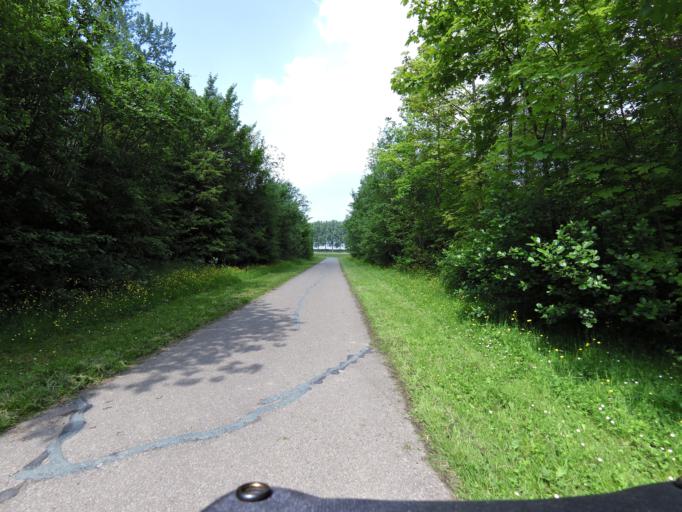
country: NL
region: South Holland
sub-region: Gemeente Spijkenisse
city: Spijkenisse
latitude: 51.8106
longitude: 4.2966
